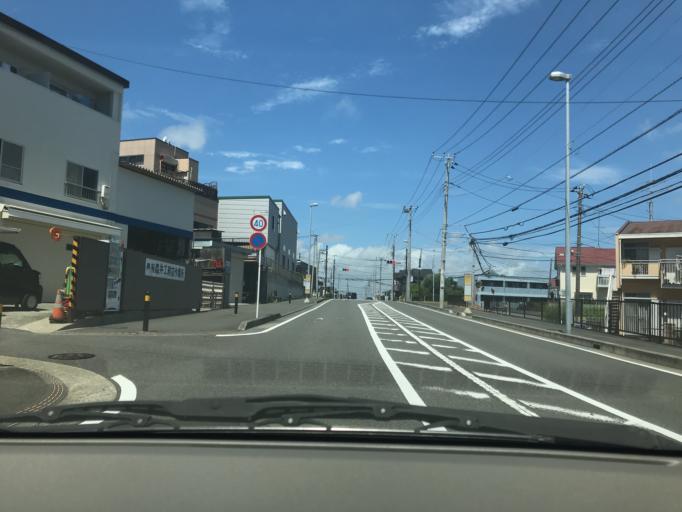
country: JP
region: Kanagawa
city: Fujisawa
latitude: 35.3630
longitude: 139.4619
